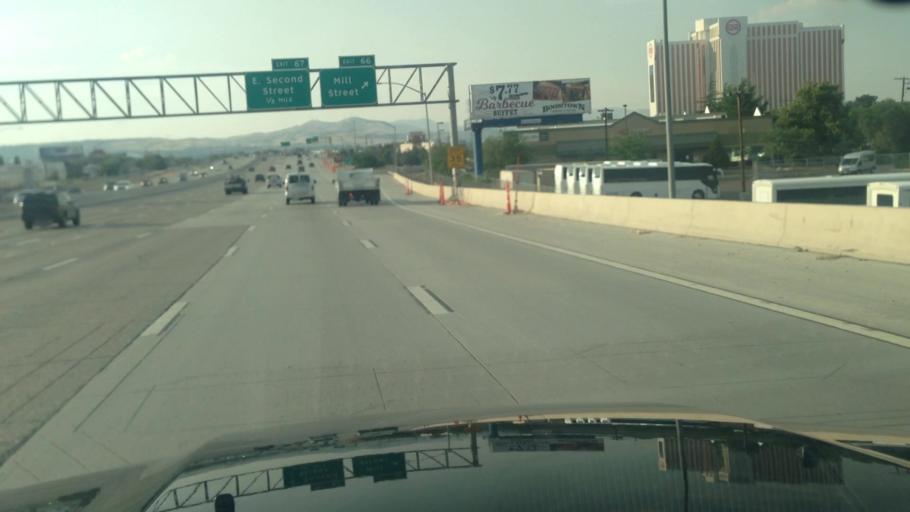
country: US
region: Nevada
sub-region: Washoe County
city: Sparks
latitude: 39.5144
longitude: -119.7814
